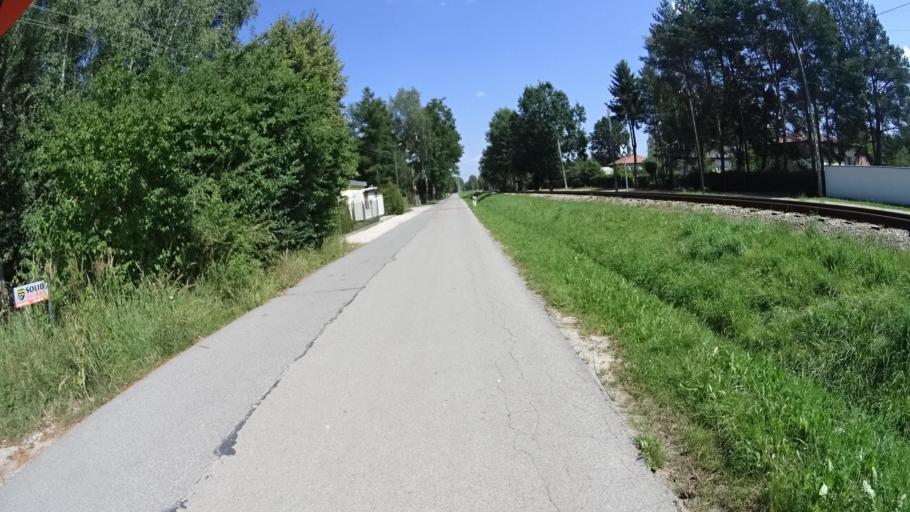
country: PL
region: Masovian Voivodeship
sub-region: Powiat piaseczynski
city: Tarczyn
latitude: 52.0008
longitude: 20.9050
